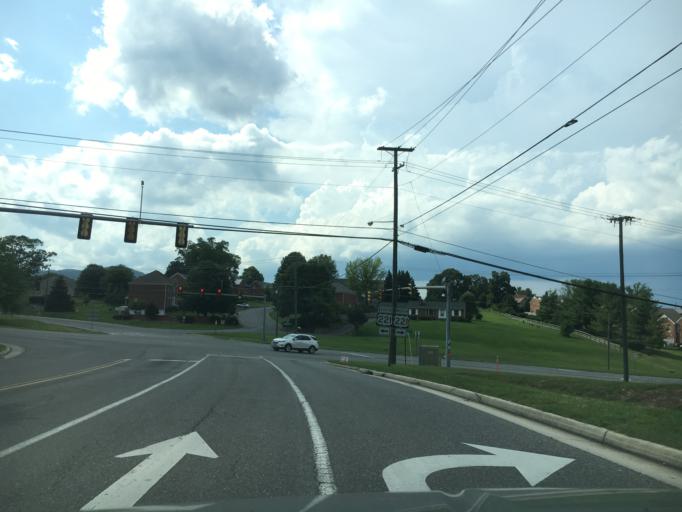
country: US
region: Virginia
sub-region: Roanoke County
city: Cave Spring
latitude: 37.2174
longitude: -80.0170
